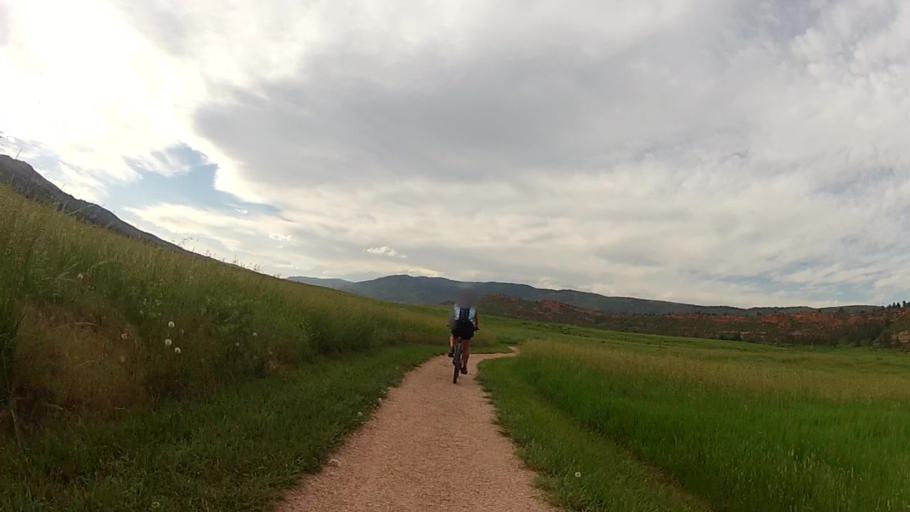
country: US
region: Colorado
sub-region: Larimer County
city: Laporte
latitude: 40.4867
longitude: -105.2328
